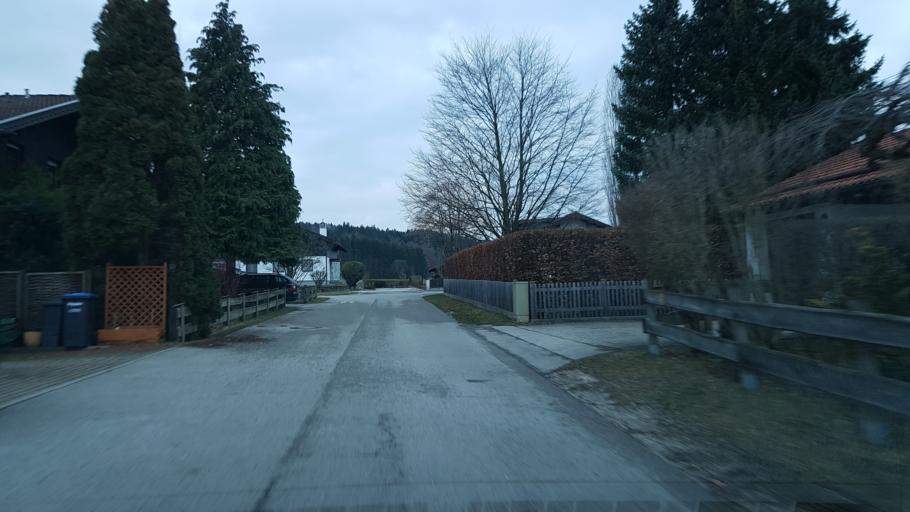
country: DE
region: Bavaria
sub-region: Upper Bavaria
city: Bernau am Chiemsee
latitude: 47.8070
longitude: 12.3763
